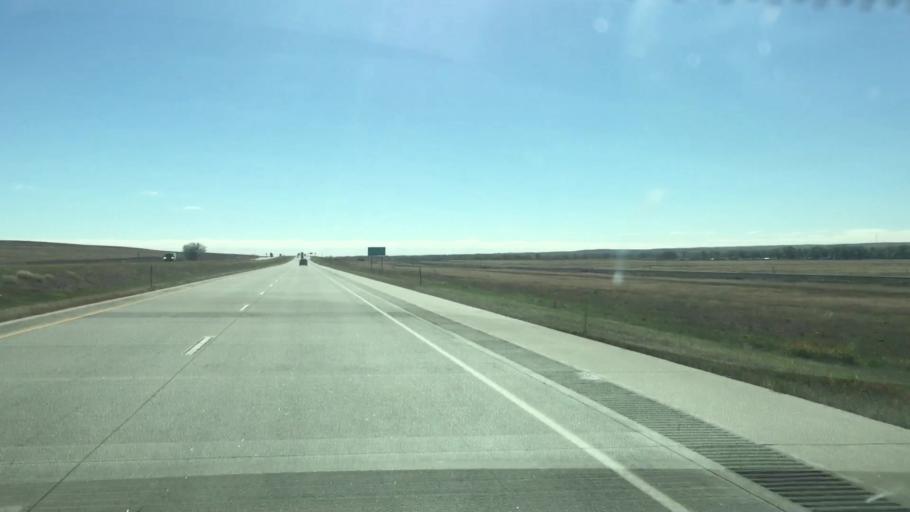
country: US
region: Colorado
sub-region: Lincoln County
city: Limon
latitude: 39.2968
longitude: -103.8052
